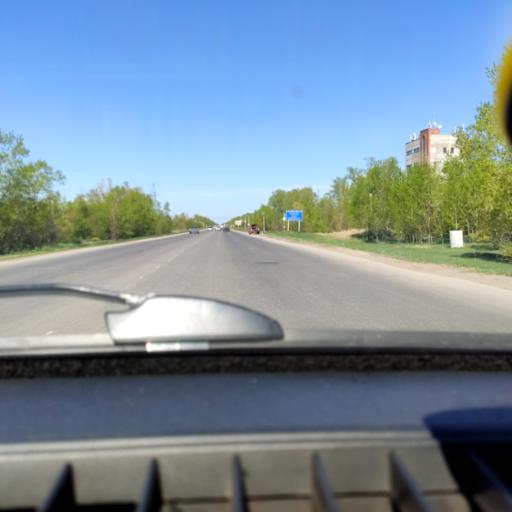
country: RU
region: Samara
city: Tol'yatti
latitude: 53.5831
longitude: 49.4042
